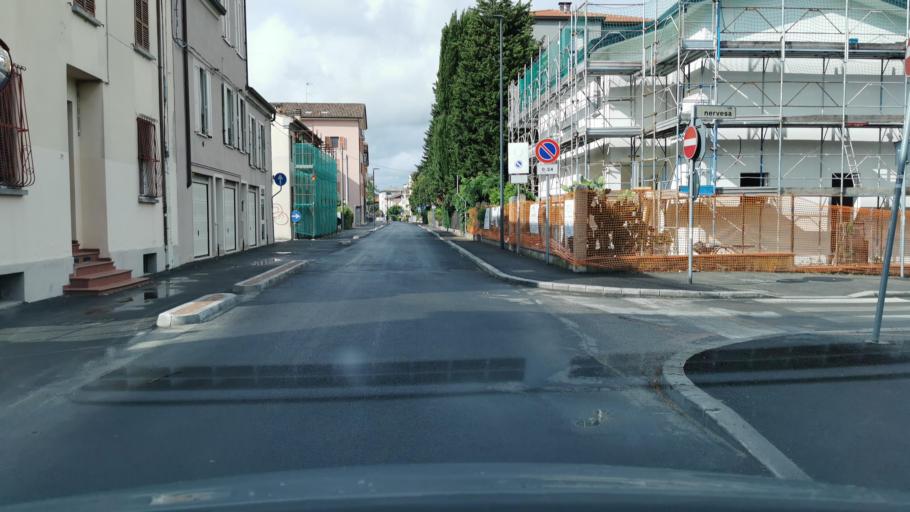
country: IT
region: Emilia-Romagna
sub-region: Provincia di Ravenna
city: Ravenna
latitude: 44.4075
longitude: 12.1990
